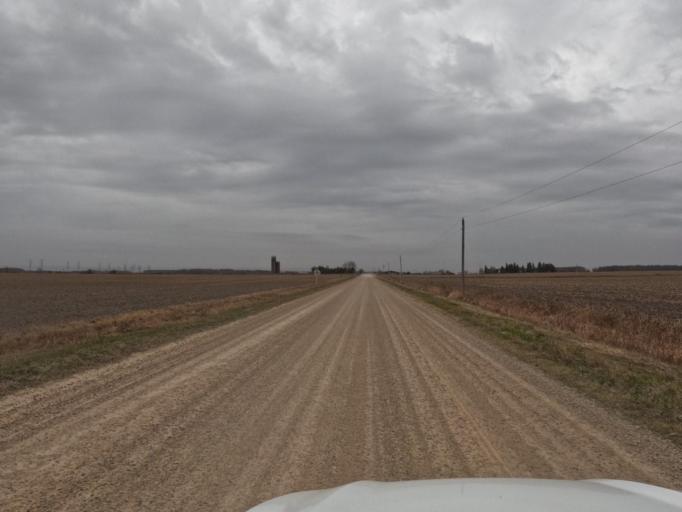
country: CA
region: Ontario
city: Shelburne
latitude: 43.8881
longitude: -80.3596
